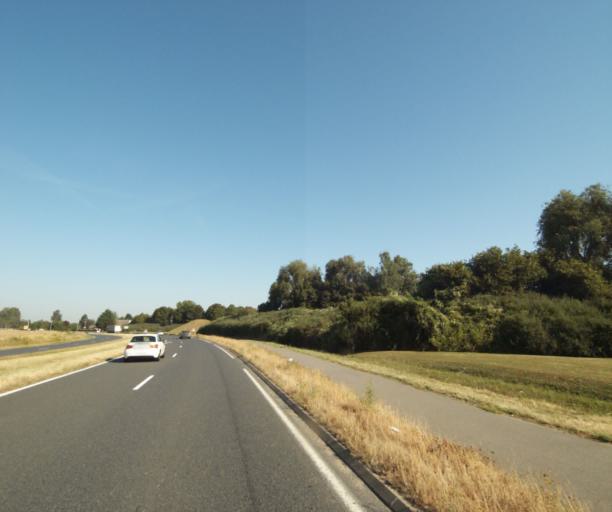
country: FR
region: Ile-de-France
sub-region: Departement de Seine-et-Marne
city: Moissy-Cramayel
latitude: 48.6244
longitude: 2.5785
